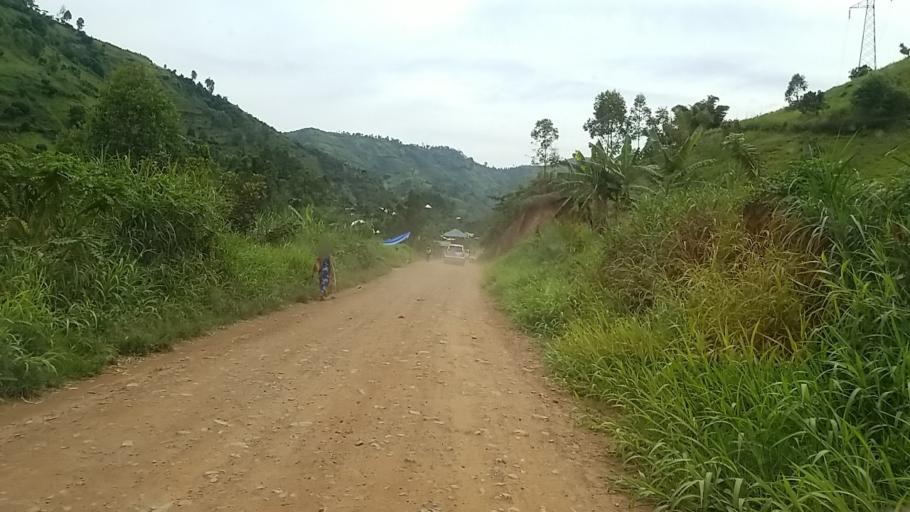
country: CD
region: Nord Kivu
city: Sake
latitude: -1.7251
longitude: 29.0108
